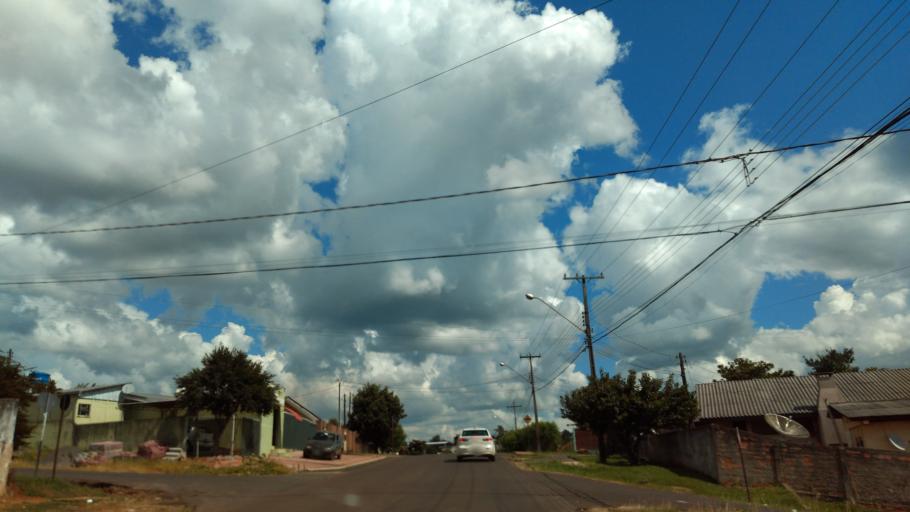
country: BR
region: Parana
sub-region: Guarapuava
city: Guarapuava
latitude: -25.4058
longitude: -51.4924
